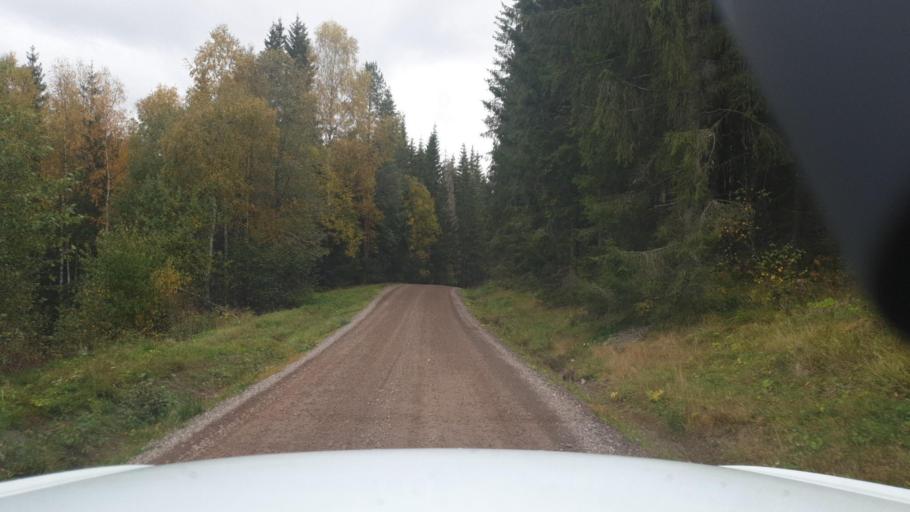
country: SE
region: Vaermland
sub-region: Eda Kommun
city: Charlottenberg
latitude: 60.0326
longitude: 12.5986
